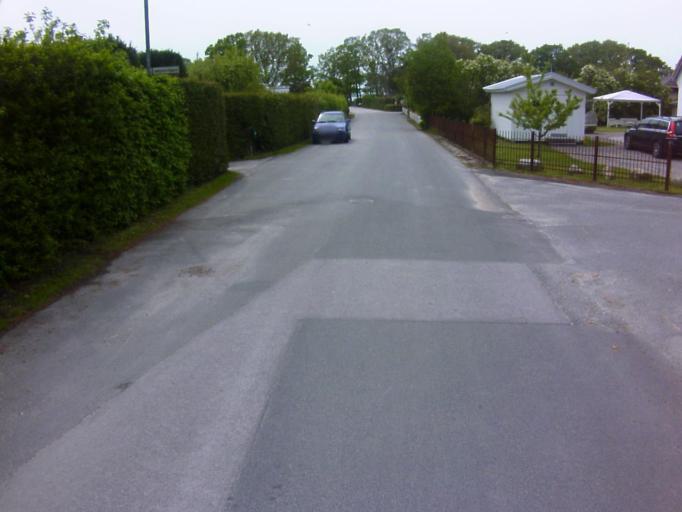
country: SE
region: Blekinge
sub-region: Solvesborgs Kommun
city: Soelvesborg
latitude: 56.0379
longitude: 14.5594
